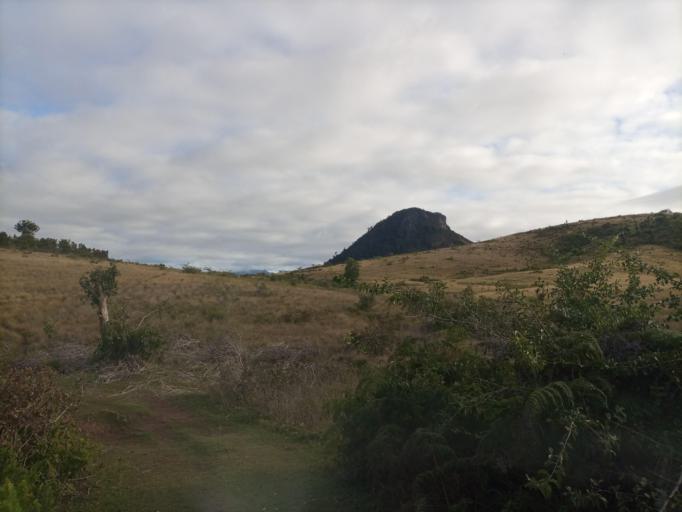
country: MG
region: Anosy
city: Fort Dauphin
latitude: -24.3124
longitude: 47.2607
